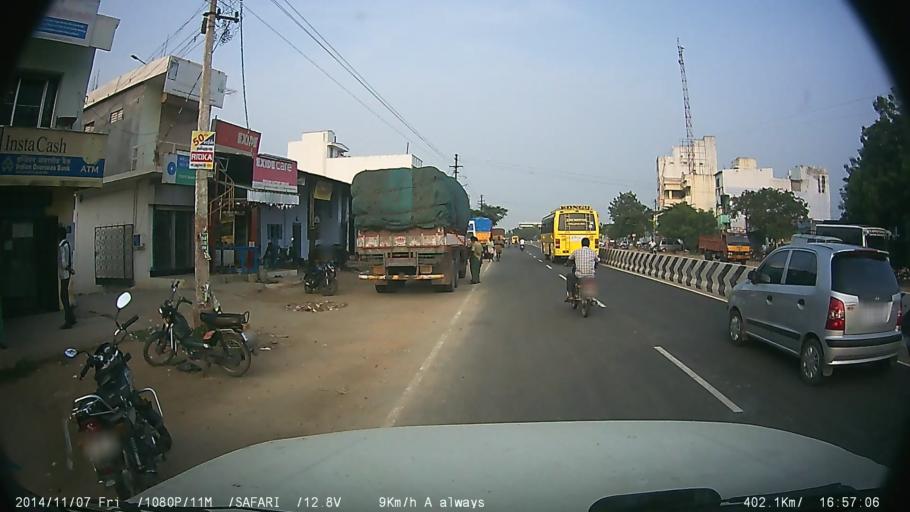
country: IN
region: Tamil Nadu
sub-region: Erode
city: Perundurai
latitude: 11.2802
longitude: 77.5868
